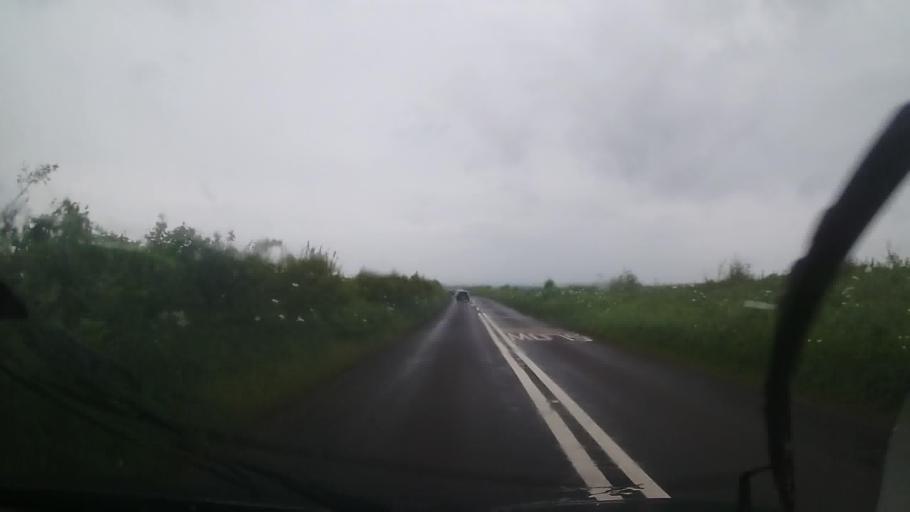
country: GB
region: England
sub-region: Devon
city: Dartmouth
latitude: 50.3855
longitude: -3.5593
